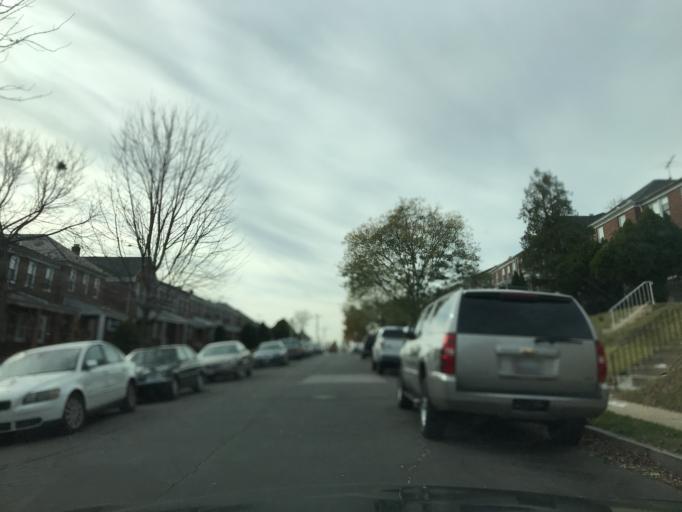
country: US
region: Maryland
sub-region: City of Baltimore
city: Baltimore
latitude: 39.3253
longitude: -76.5756
